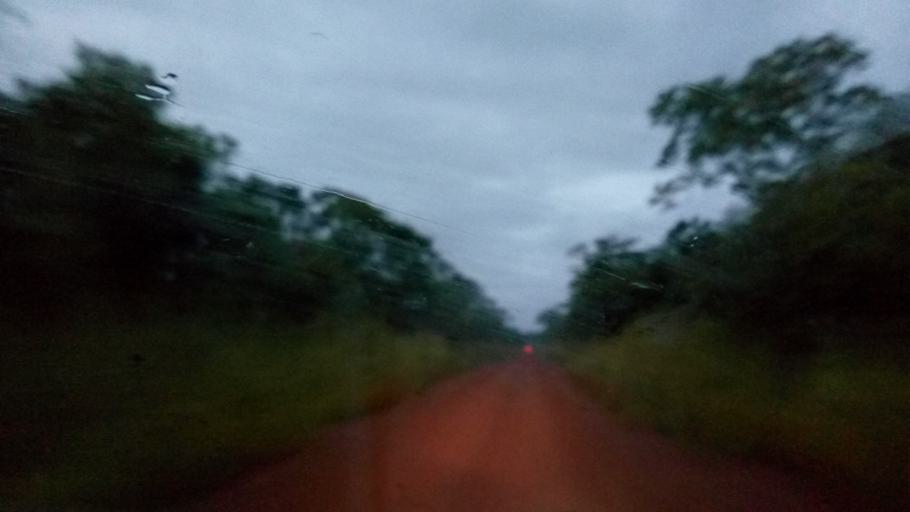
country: ZM
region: Luapula
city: Nchelenge
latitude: -9.8076
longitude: 28.1429
